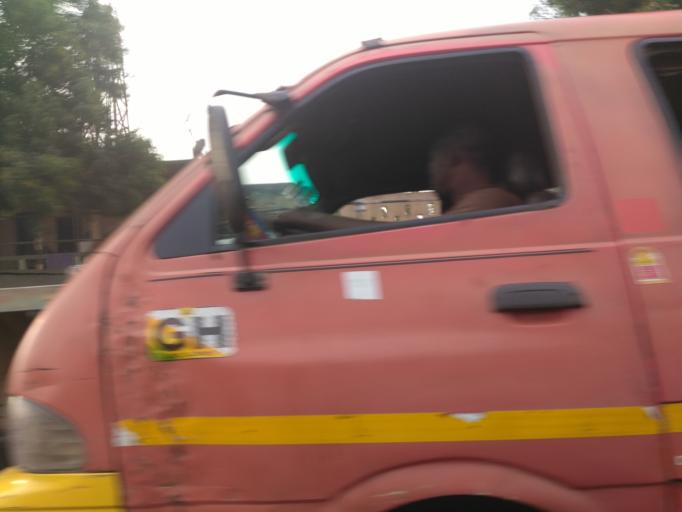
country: GH
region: Ashanti
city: Kumasi
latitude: 6.6883
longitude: -1.5926
